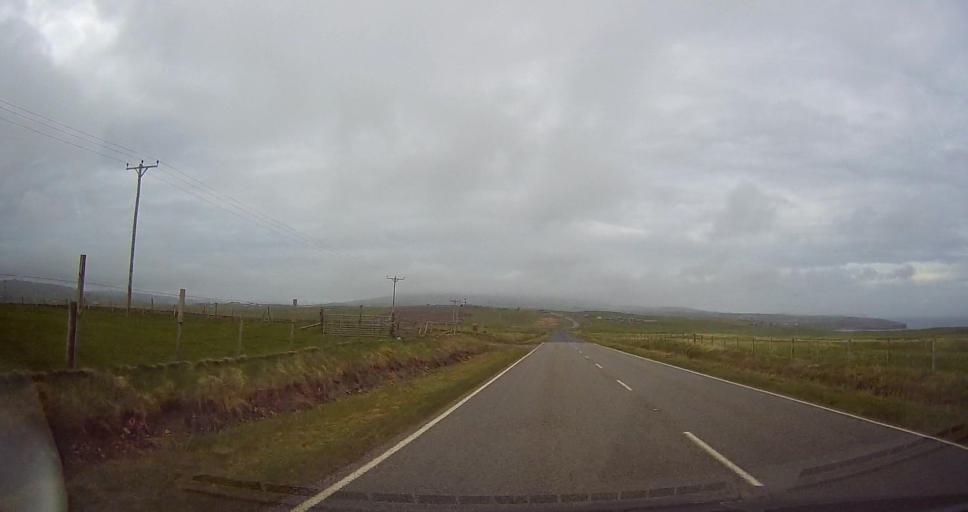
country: GB
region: Scotland
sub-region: Shetland Islands
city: Sandwick
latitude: 59.9007
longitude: -1.3032
